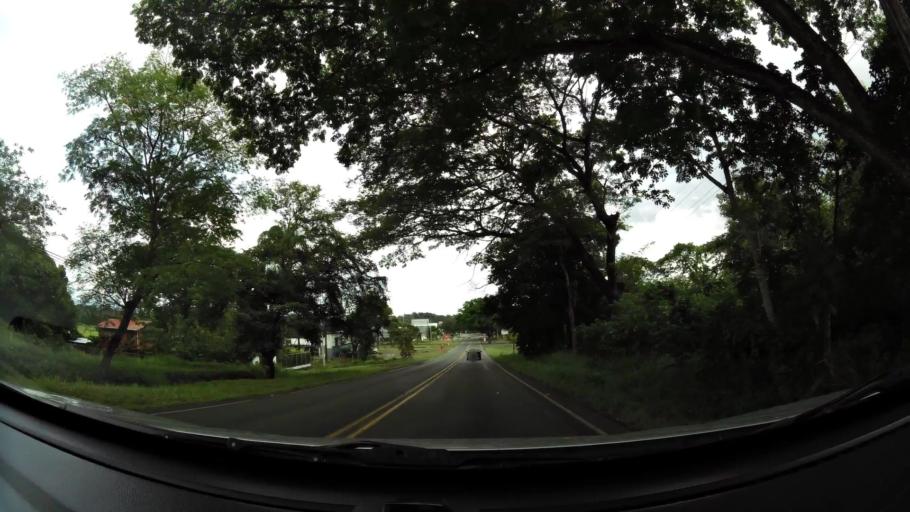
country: CR
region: Guanacaste
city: Juntas
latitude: 10.2605
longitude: -85.0172
